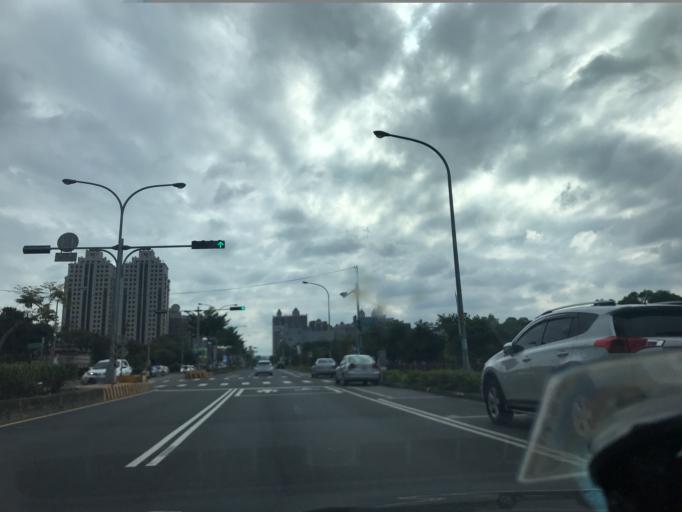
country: TW
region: Taiwan
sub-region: Hsinchu
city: Zhubei
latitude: 24.8254
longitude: 121.0243
